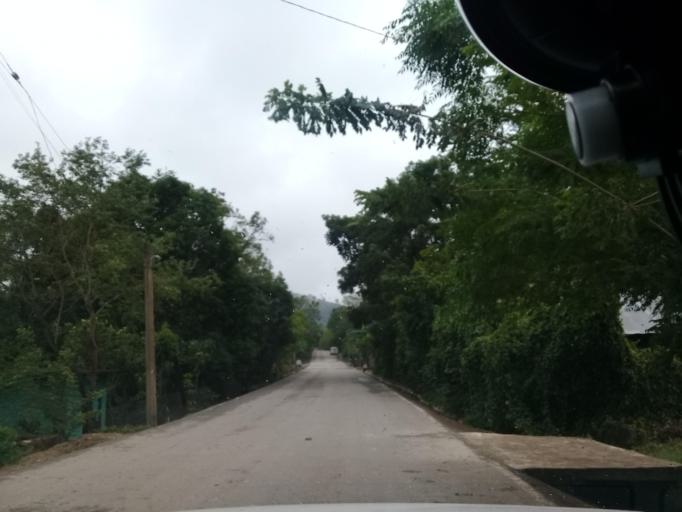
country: MX
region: Veracruz
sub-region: Chalma
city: San Pedro Coyutla
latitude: 21.2230
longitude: -98.4319
